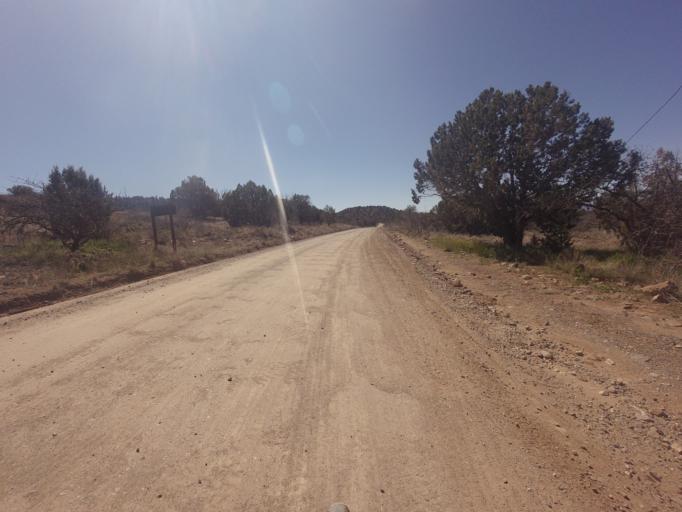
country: US
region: Arizona
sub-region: Yavapai County
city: Lake Montezuma
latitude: 34.6675
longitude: -111.7129
